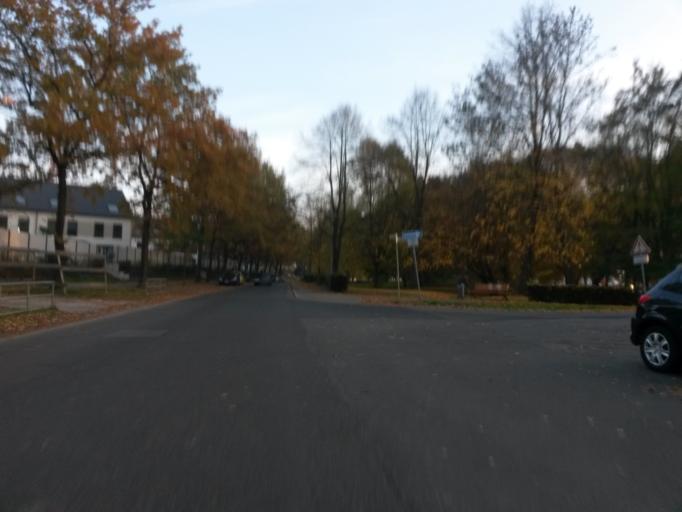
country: DE
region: Bremen
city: Bremen
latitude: 53.0539
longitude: 8.8196
